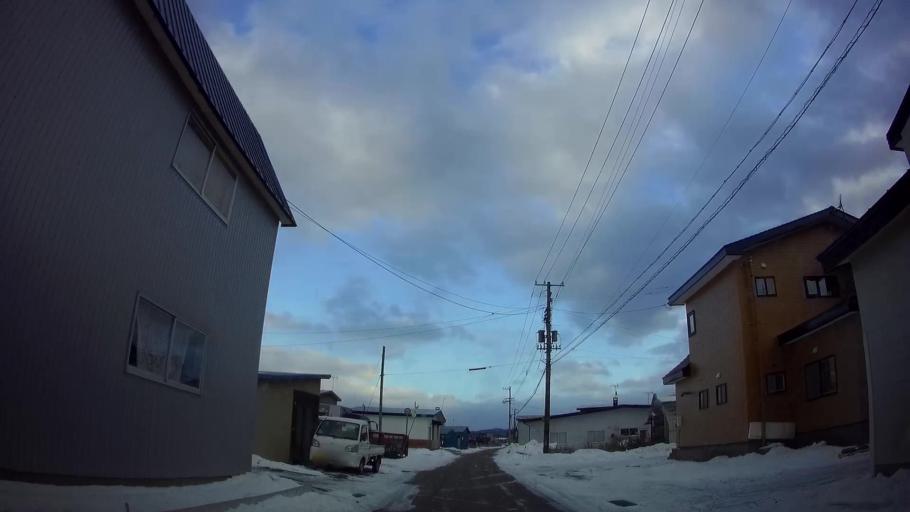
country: JP
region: Hokkaido
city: Nanae
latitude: 42.0428
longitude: 140.8135
